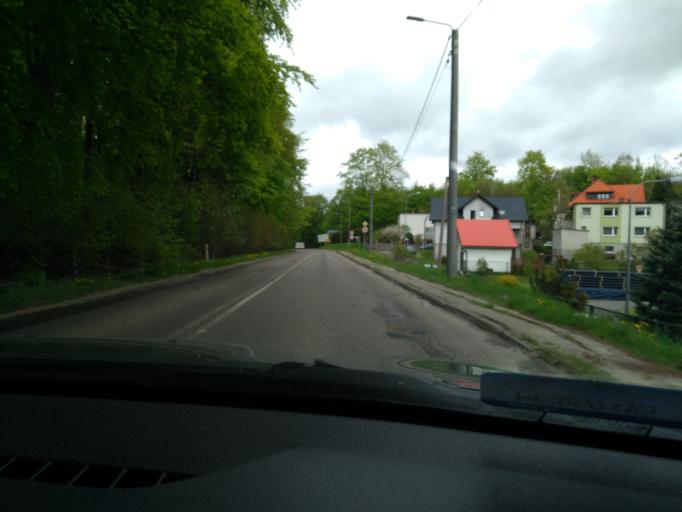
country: PL
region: Pomeranian Voivodeship
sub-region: Powiat kartuski
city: Kartuzy
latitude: 54.3405
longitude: 18.1817
